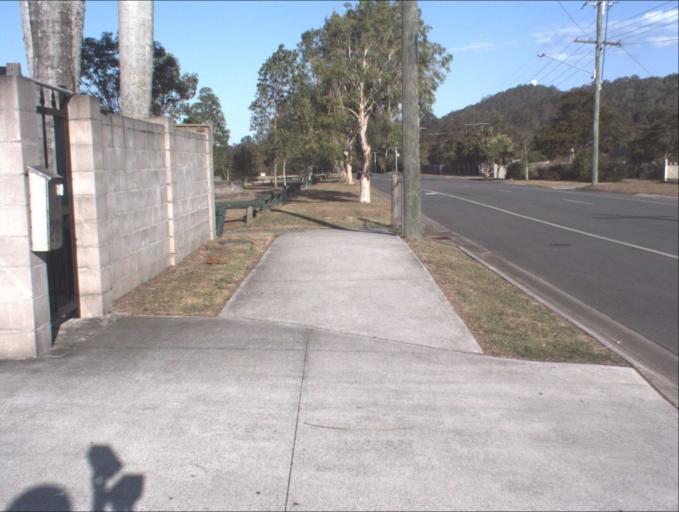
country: AU
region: Queensland
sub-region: Gold Coast
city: Yatala
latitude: -27.7116
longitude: 153.2238
